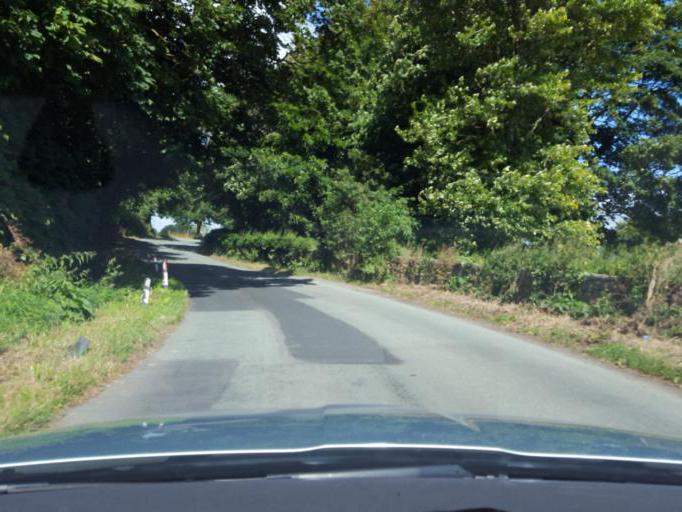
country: GB
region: Wales
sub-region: County of Flintshire
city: Mold
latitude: 53.1302
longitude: -3.1397
